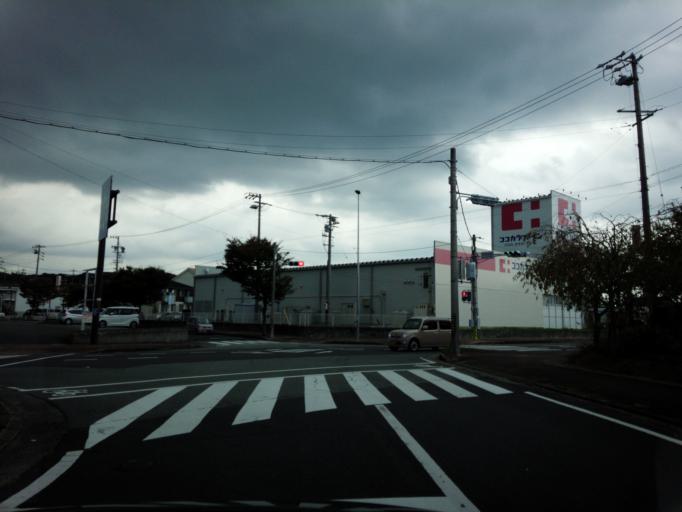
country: JP
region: Mie
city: Toba
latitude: 34.3282
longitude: 136.8203
